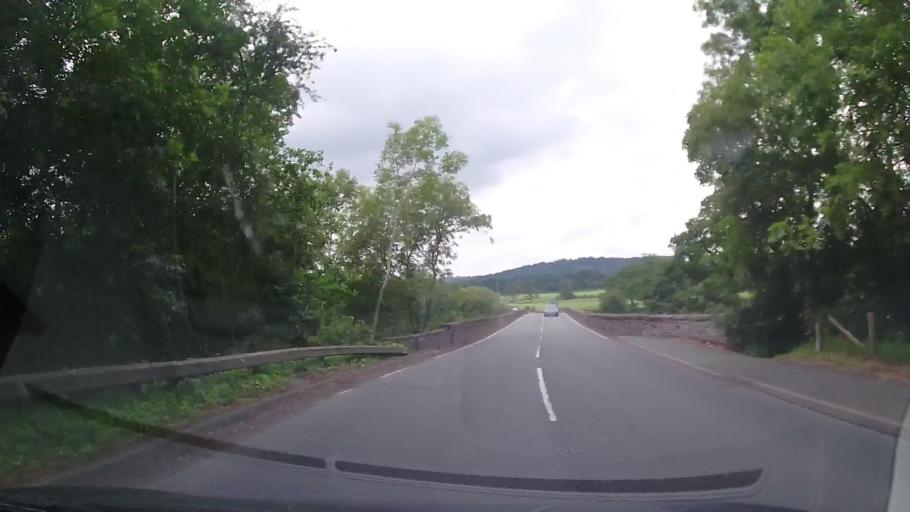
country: GB
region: Wales
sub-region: Denbighshire
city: Corwen
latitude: 52.9797
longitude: -3.3868
